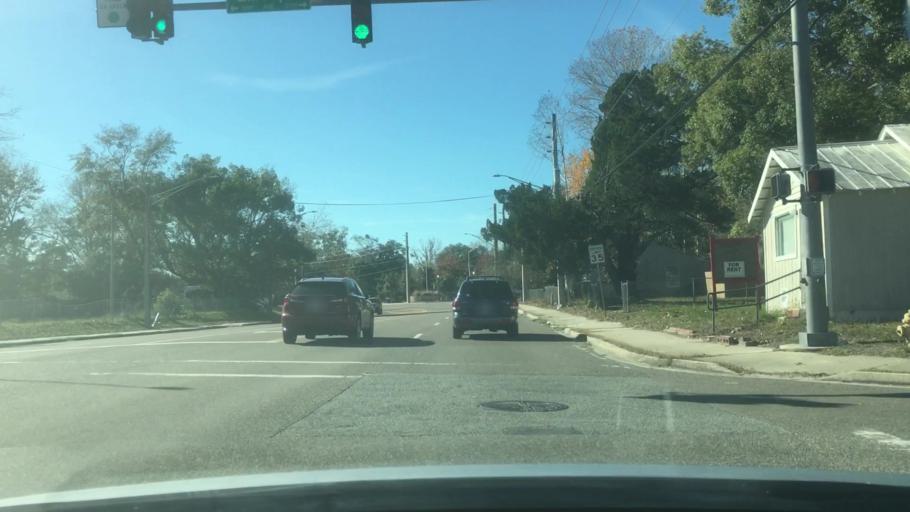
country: US
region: Florida
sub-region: Duval County
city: Jacksonville
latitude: 30.4667
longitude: -81.6261
